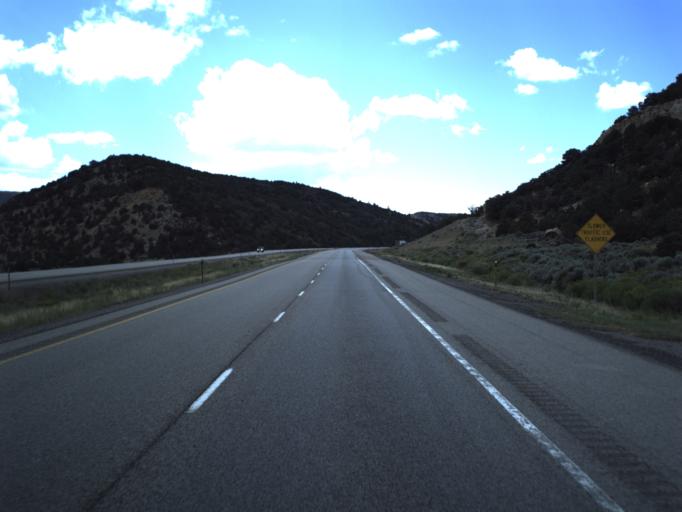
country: US
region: Utah
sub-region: Wayne County
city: Loa
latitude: 38.7616
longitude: -111.4583
